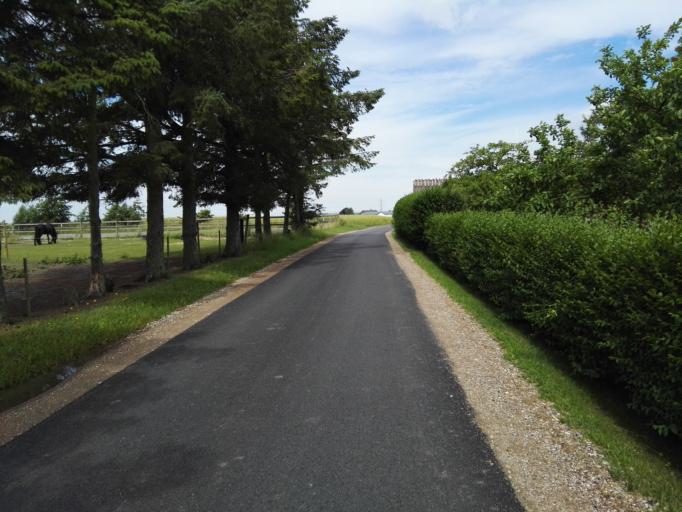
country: DK
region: Capital Region
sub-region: Egedal Kommune
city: Olstykke
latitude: 55.8159
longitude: 12.1738
